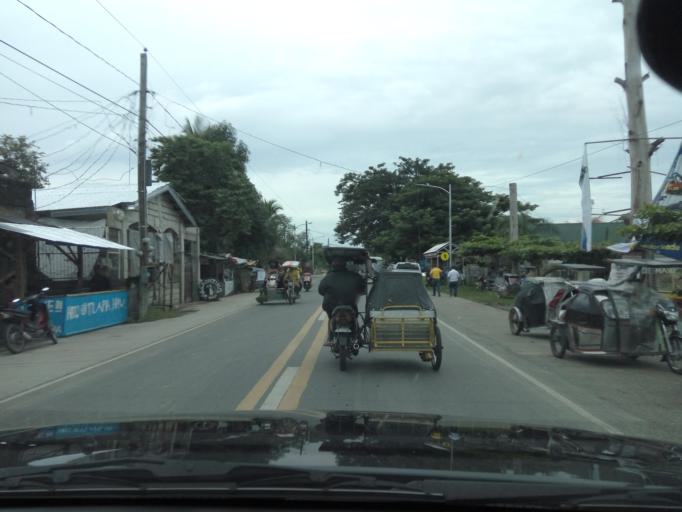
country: PH
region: Central Luzon
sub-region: Province of Nueva Ecija
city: Carmen
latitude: 15.4460
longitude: 120.8277
